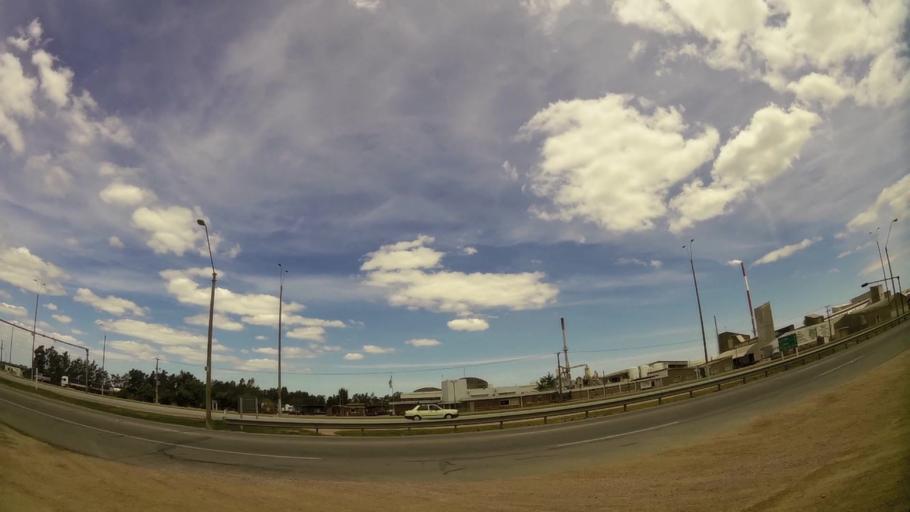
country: UY
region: San Jose
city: Delta del Tigre
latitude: -34.7757
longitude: -56.3709
